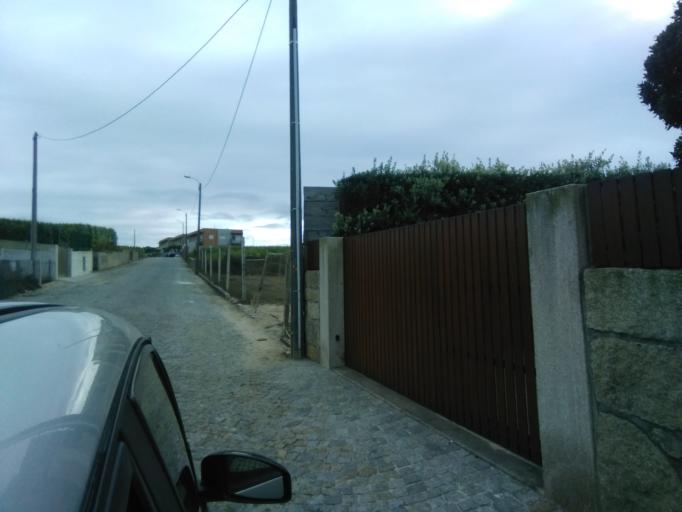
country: PT
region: Porto
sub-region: Matosinhos
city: Lavra
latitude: 41.2893
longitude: -8.7319
